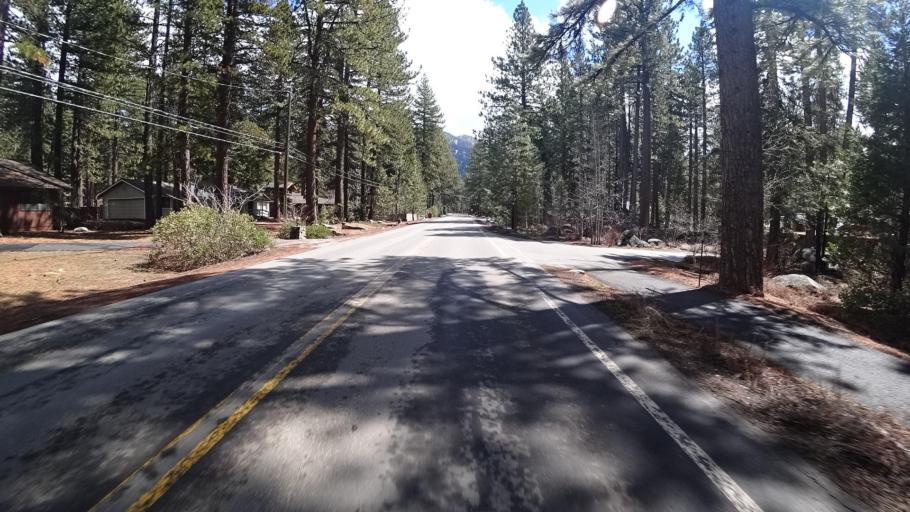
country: US
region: Nevada
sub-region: Washoe County
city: Incline Village
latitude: 39.2388
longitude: -119.9411
